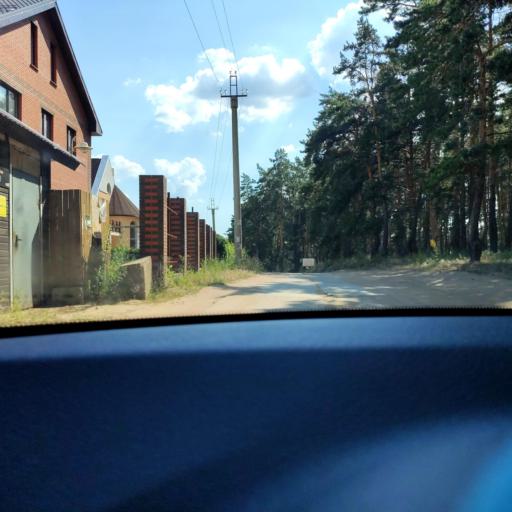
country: RU
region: Samara
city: Volzhskiy
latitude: 53.4405
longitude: 50.1684
